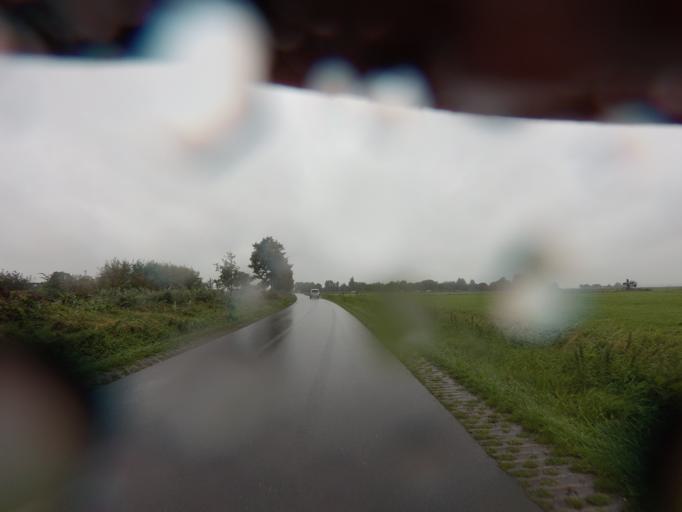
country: NL
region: North Holland
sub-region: Gemeente Medemblik
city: Opperdoes
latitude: 52.7300
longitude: 5.1043
